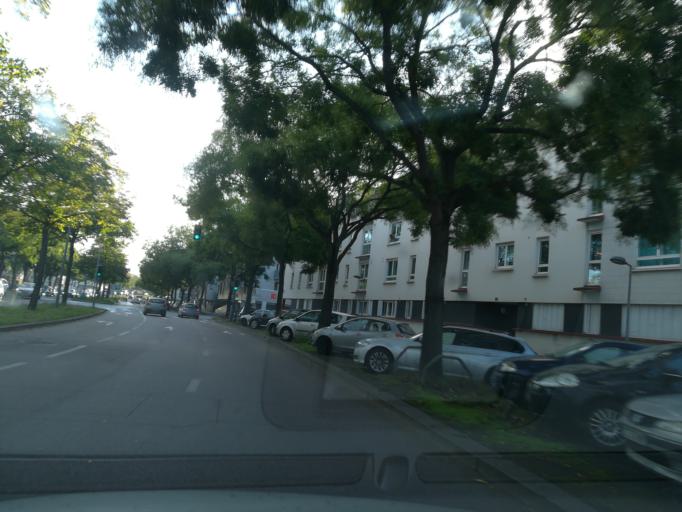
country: FR
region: Haute-Normandie
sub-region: Departement de la Seine-Maritime
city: Rouen
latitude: 49.4289
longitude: 1.0953
